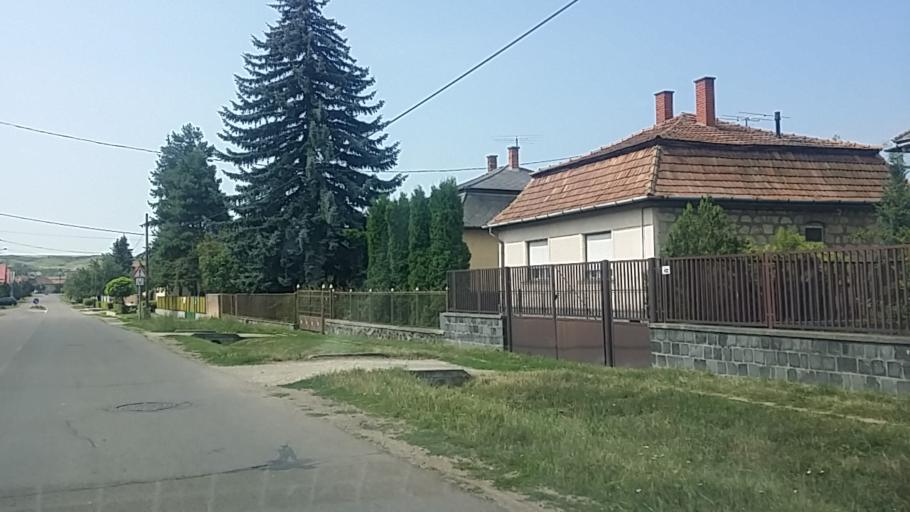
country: HU
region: Nograd
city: Tar
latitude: 47.9548
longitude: 19.7461
